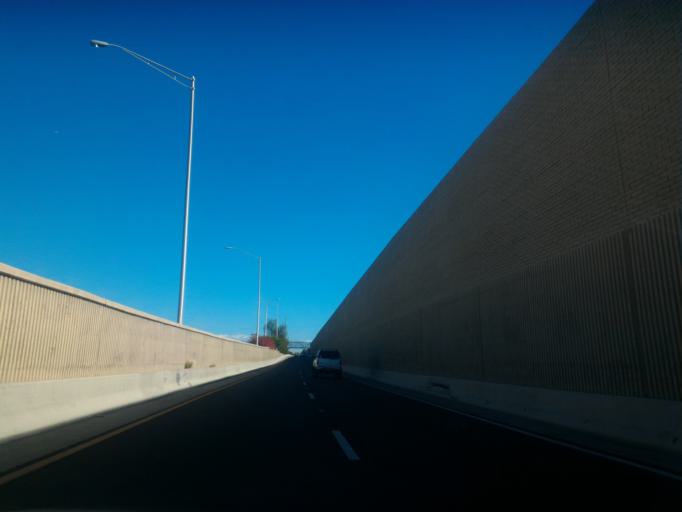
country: US
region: Arizona
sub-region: Maricopa County
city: Tempe
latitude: 33.3854
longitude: -111.9053
